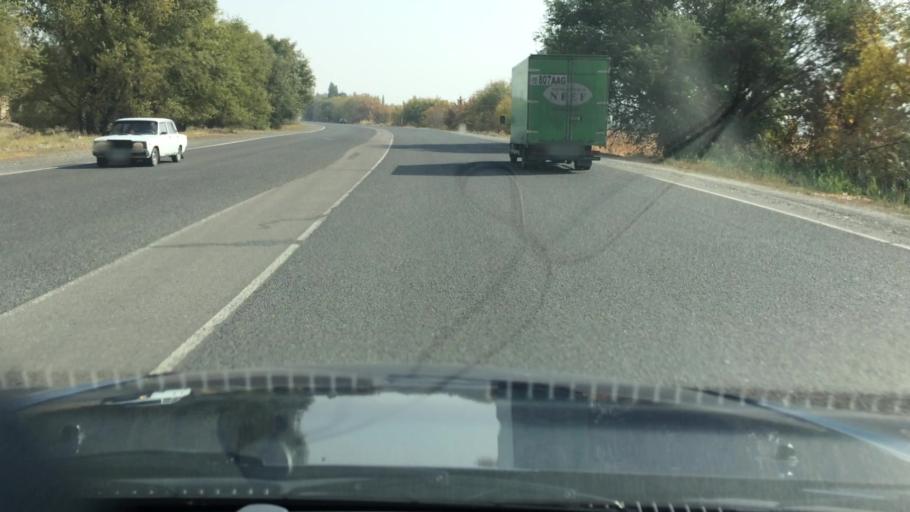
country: KG
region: Chuy
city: Ivanovka
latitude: 42.9399
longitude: 74.9716
